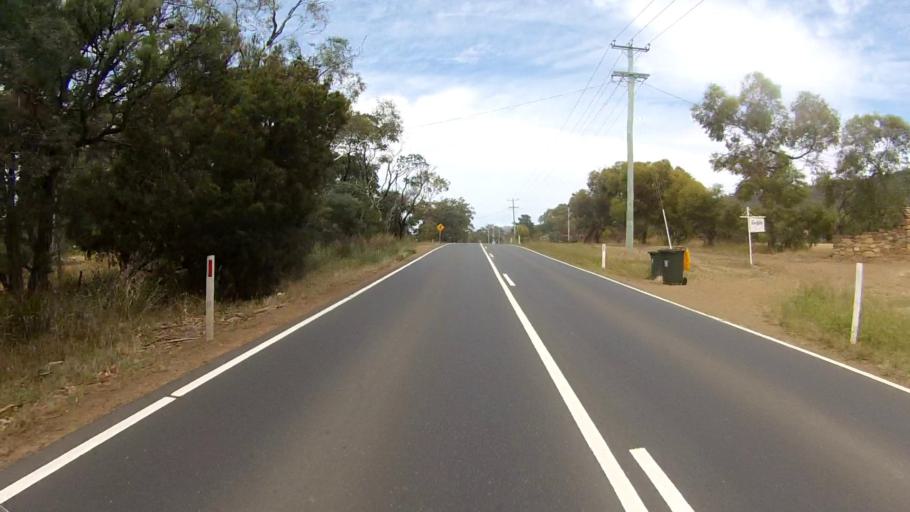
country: AU
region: Tasmania
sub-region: Clarence
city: Acton Park
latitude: -42.8861
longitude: 147.4831
